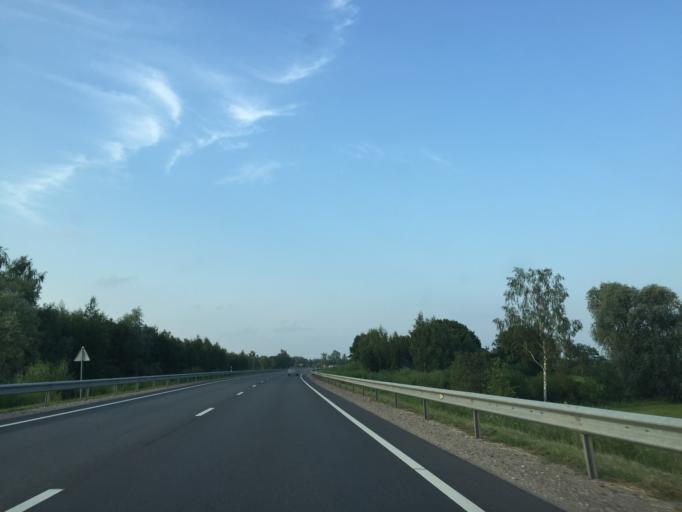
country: LV
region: Ozolnieku
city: Ozolnieki
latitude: 56.6407
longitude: 23.7775
